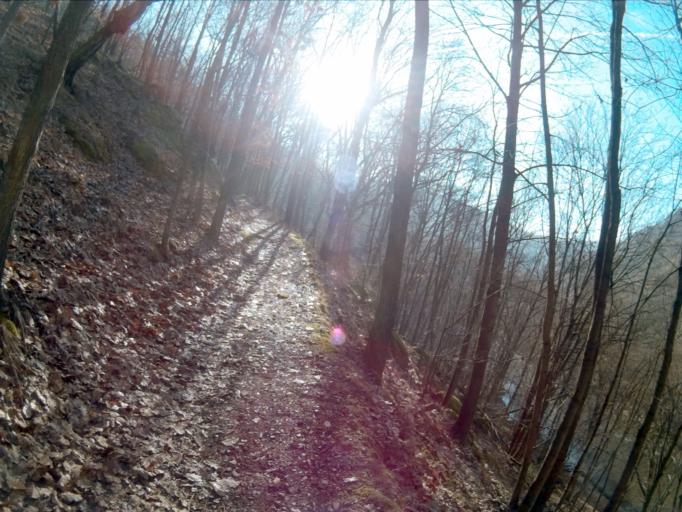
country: CZ
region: Vysocina
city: Namest' nad Oslavou
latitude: 49.1643
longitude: 16.1688
